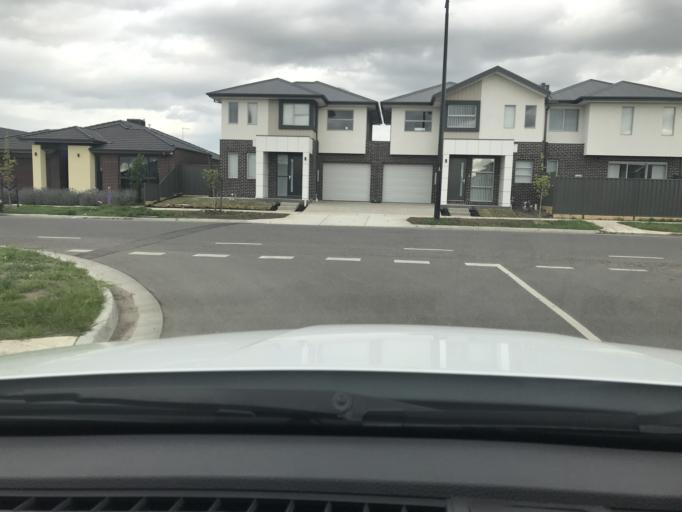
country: AU
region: Victoria
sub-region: Hume
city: Roxburgh Park
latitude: -37.6001
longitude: 144.8927
